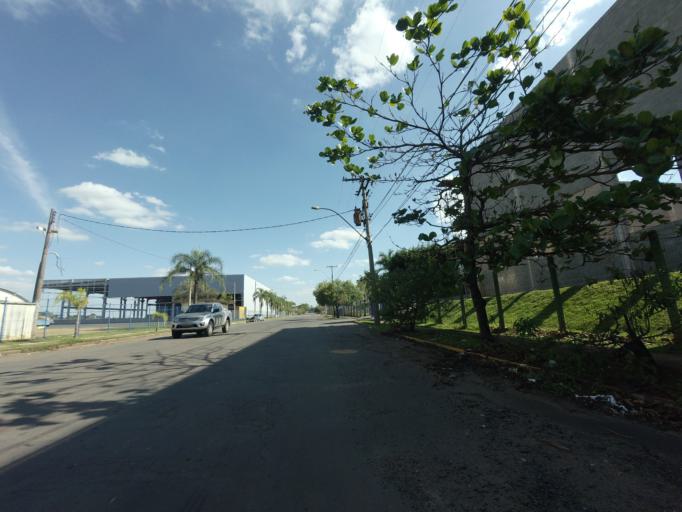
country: BR
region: Sao Paulo
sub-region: Piracicaba
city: Piracicaba
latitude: -22.7266
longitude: -47.5955
